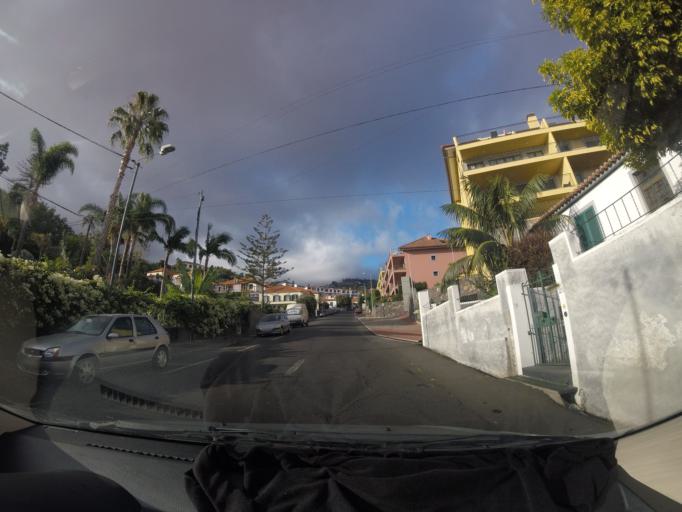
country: PT
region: Madeira
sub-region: Funchal
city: Nossa Senhora do Monte
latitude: 32.6559
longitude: -16.9094
